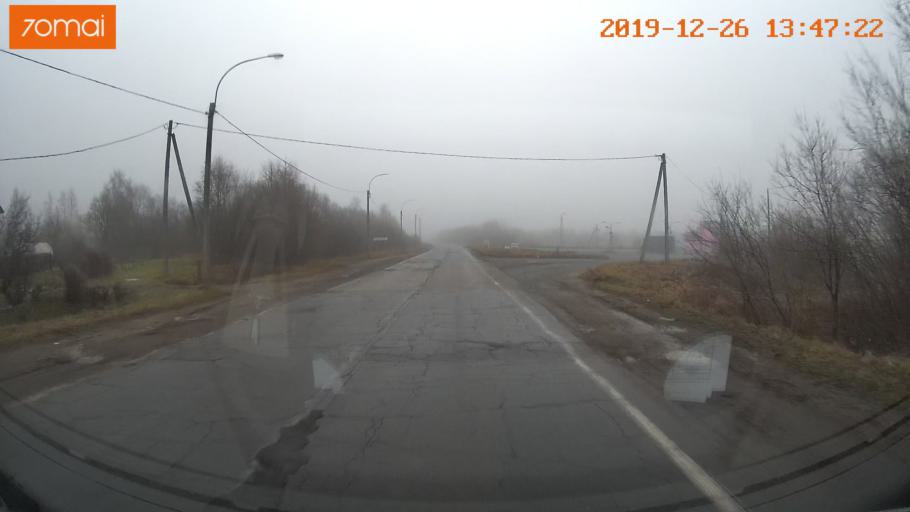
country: RU
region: Vologda
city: Sheksna
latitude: 58.6853
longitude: 38.5335
